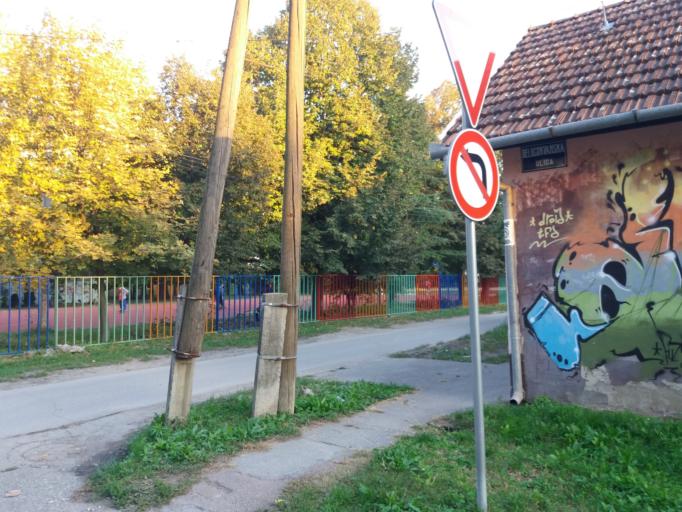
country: RS
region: Autonomna Pokrajina Vojvodina
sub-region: Severnobacki Okrug
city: Subotica
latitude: 46.1036
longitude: 19.6815
